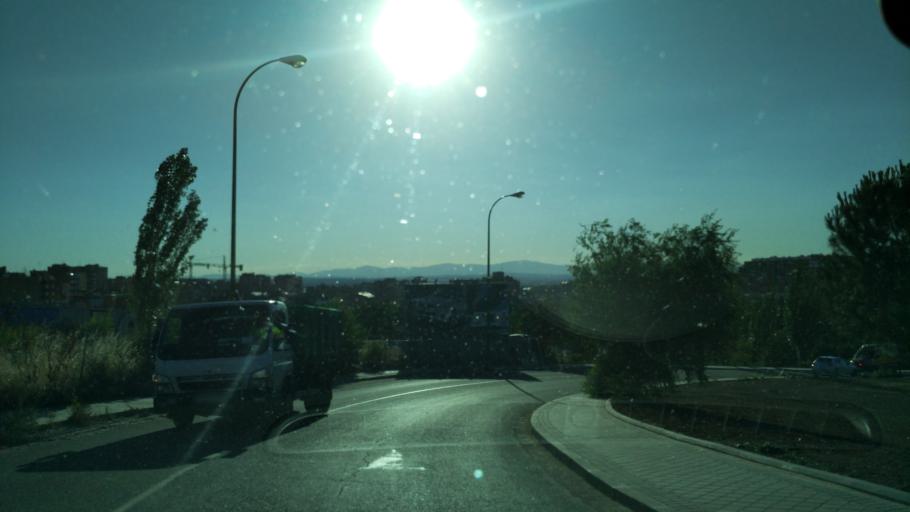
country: ES
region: Madrid
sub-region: Provincia de Madrid
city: Tetuan de las Victorias
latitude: 40.4686
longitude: -3.7093
